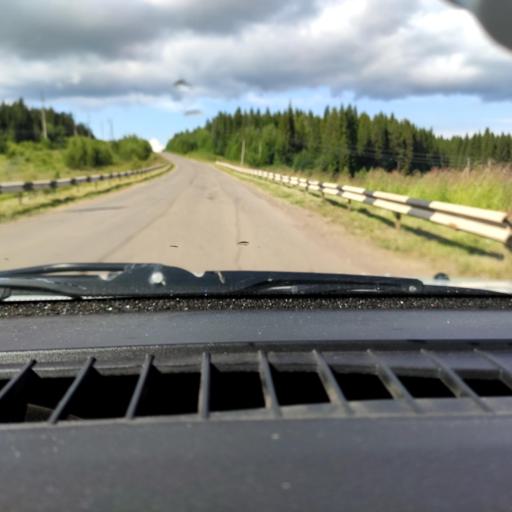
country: RU
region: Perm
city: Uinskoye
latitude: 57.1179
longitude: 56.5501
